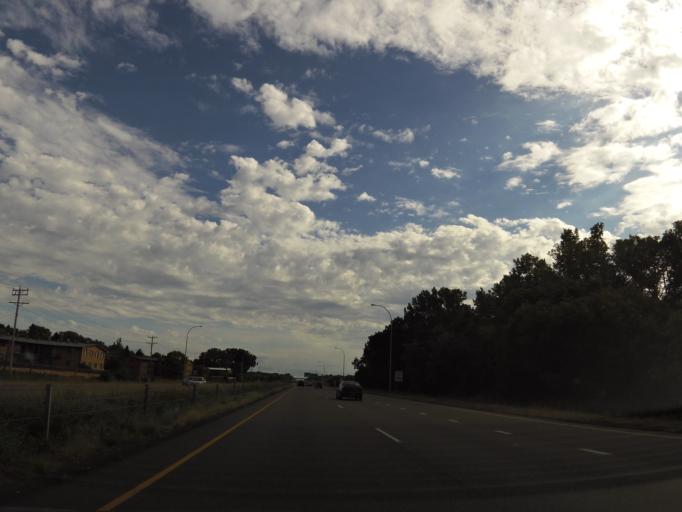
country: US
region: Minnesota
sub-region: Hennepin County
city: New Hope
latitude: 45.0403
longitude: -93.4008
